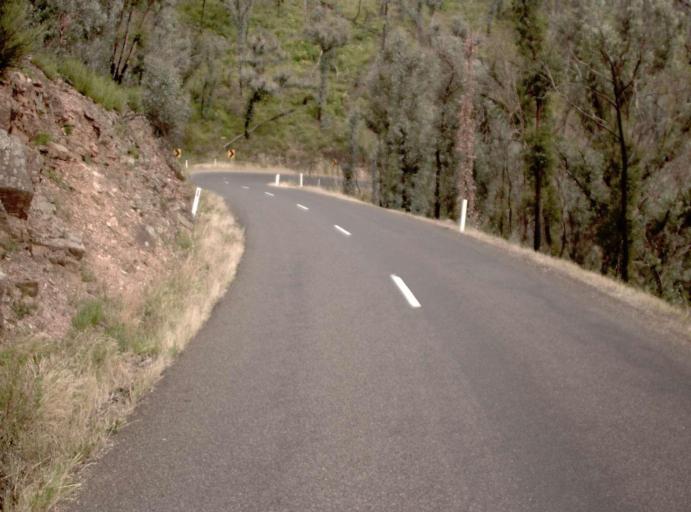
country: AU
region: Victoria
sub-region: Wellington
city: Heyfield
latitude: -37.8133
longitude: 146.6727
